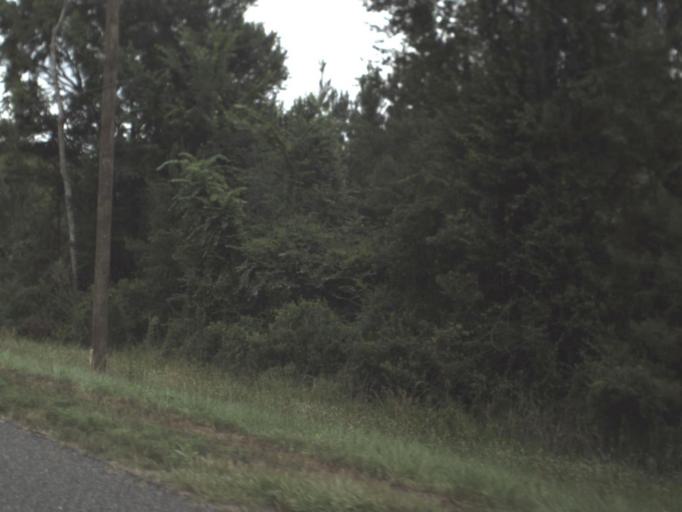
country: US
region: Florida
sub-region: Nassau County
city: Callahan
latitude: 30.6328
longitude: -81.8546
